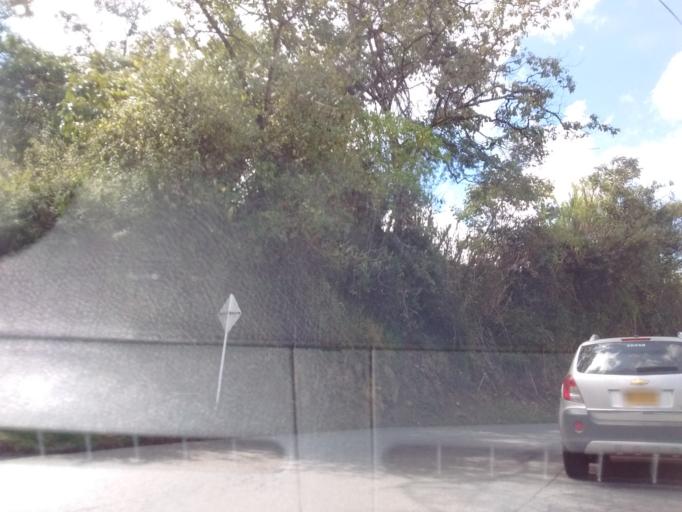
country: CO
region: Antioquia
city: Medellin
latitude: 6.2443
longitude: -75.5138
